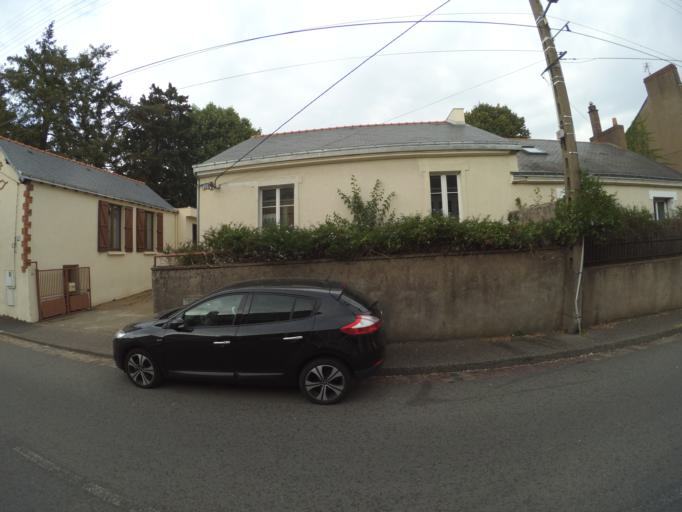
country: FR
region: Pays de la Loire
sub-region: Departement de la Loire-Atlantique
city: Reze
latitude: 47.1865
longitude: -1.5279
